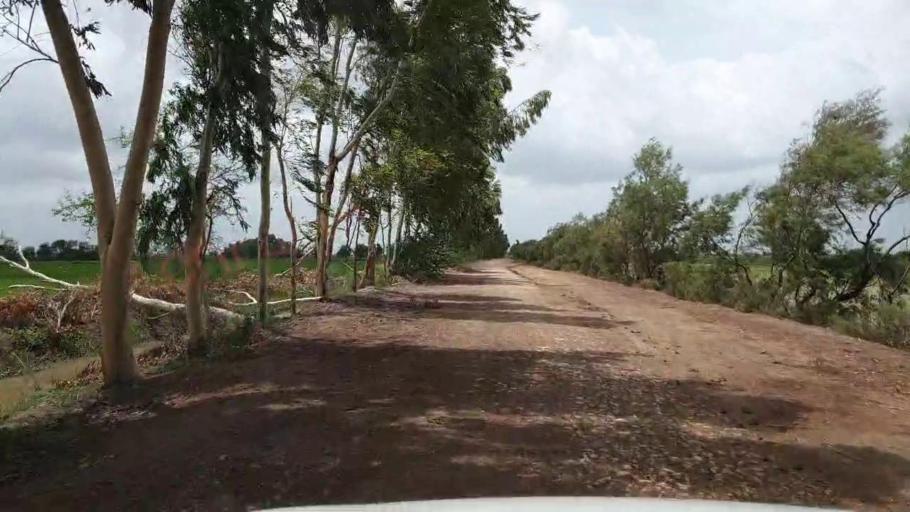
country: PK
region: Sindh
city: Kario
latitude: 24.7416
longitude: 68.5187
